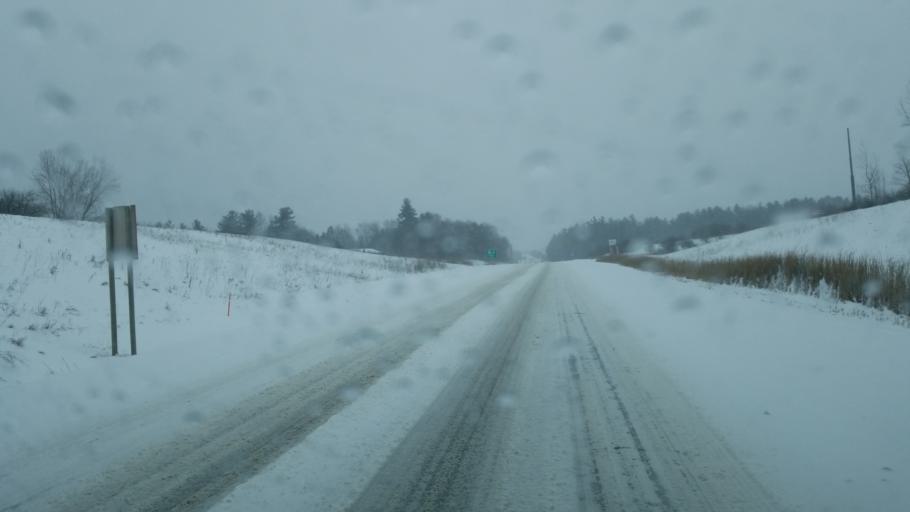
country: US
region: Michigan
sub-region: Mecosta County
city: Big Rapids
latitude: 43.5836
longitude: -85.4887
